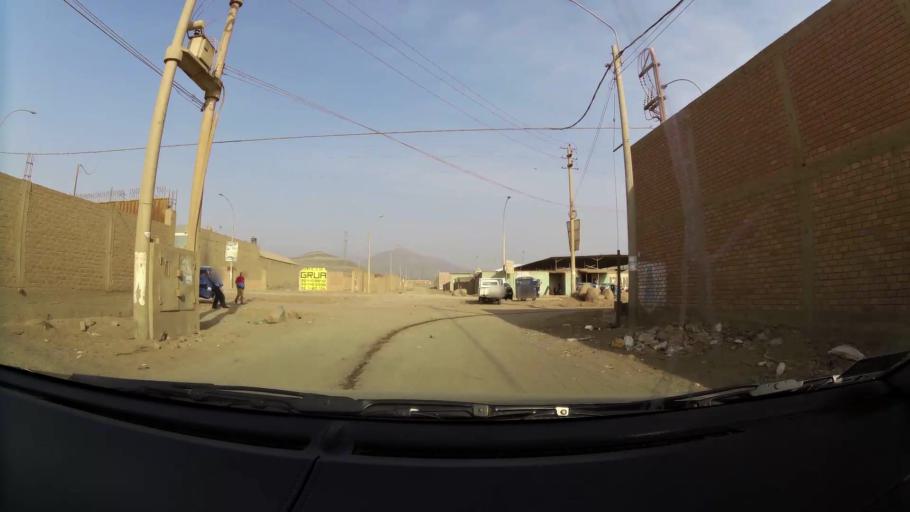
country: PE
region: Lima
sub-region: Lima
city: Santa Rosa
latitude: -11.7573
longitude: -77.1565
